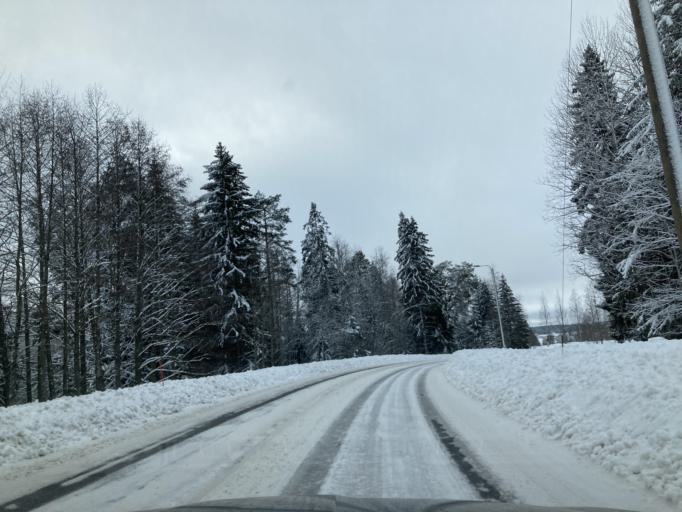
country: FI
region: Central Finland
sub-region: Jaemsae
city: Jaemsae
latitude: 61.8622
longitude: 25.2351
